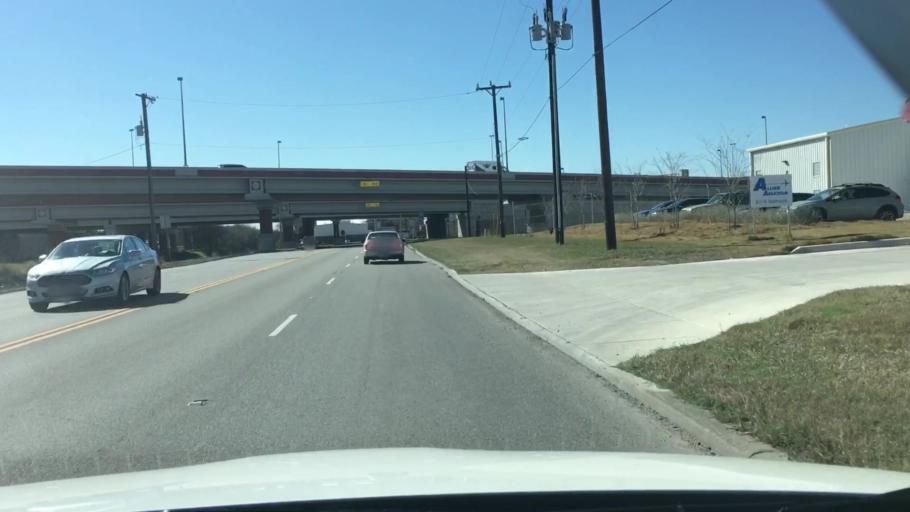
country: US
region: Texas
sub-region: Bexar County
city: Alamo Heights
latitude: 29.5196
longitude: -98.4682
